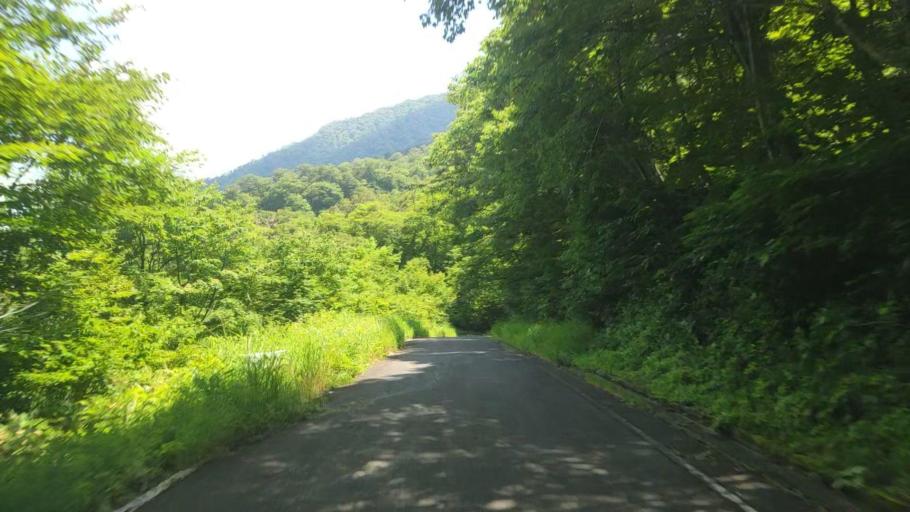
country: JP
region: Fukui
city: Ono
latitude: 35.7740
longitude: 136.5283
